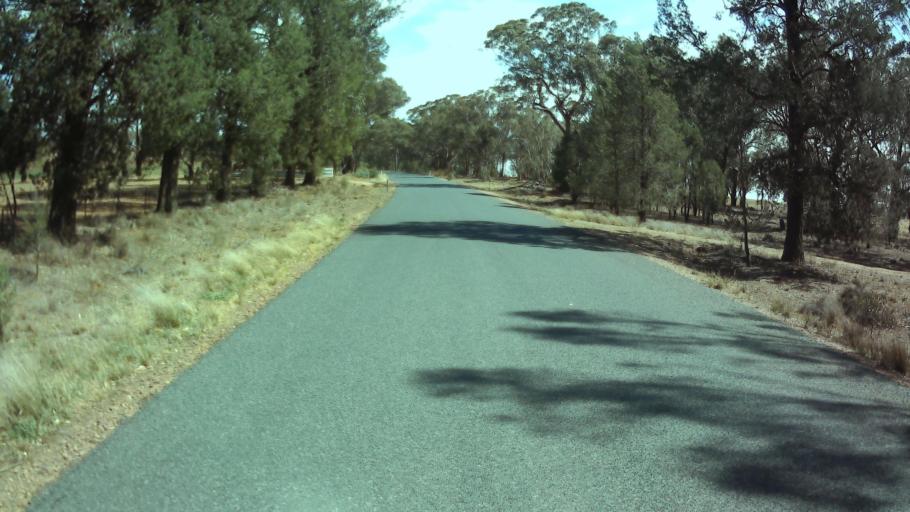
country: AU
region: New South Wales
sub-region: Weddin
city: Grenfell
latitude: -34.0469
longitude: 148.1313
